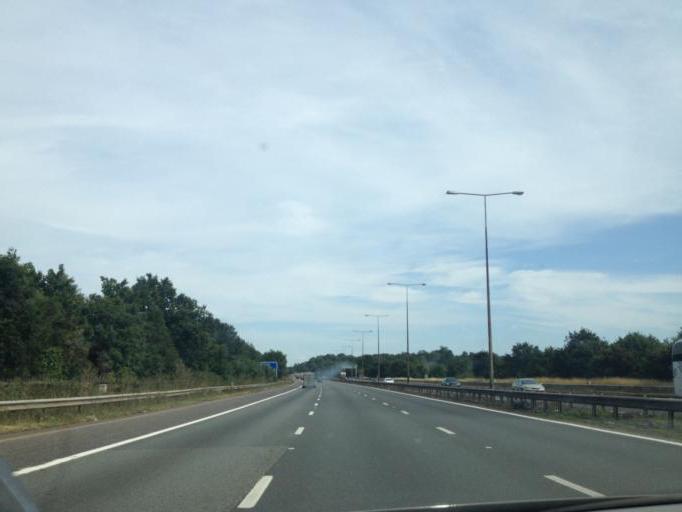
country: GB
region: England
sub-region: Hertfordshire
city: Elstree
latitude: 51.6404
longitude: -0.3175
